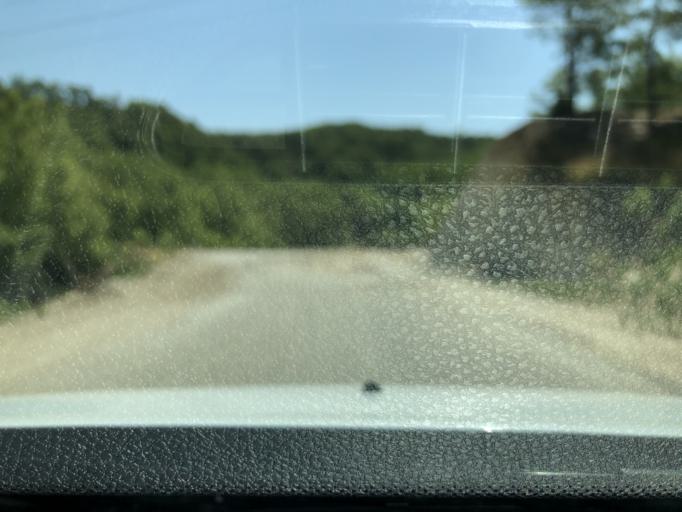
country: TR
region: Antalya
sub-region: Manavgat
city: Manavgat
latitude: 36.8335
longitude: 31.5303
